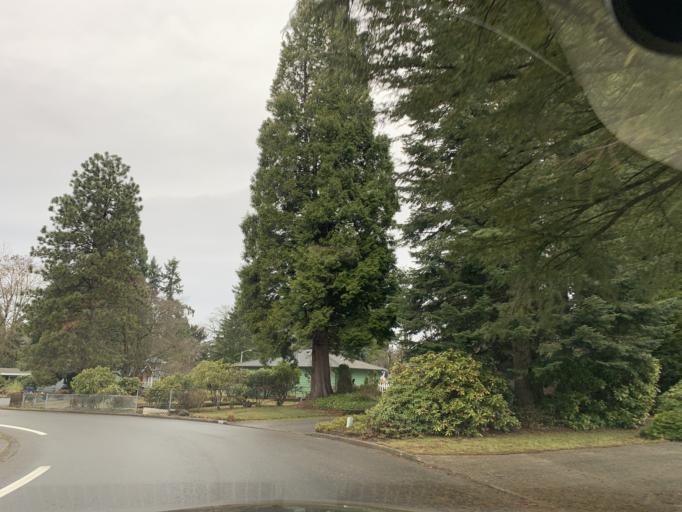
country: US
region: Washington
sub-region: King County
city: Woodinville
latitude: 47.7404
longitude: -122.1699
